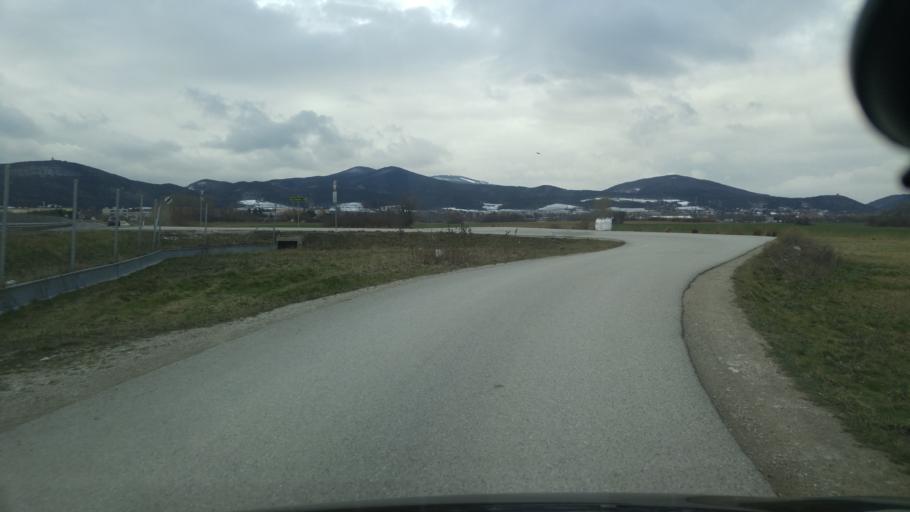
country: AT
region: Lower Austria
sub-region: Politischer Bezirk Baden
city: Bad Voslau
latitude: 47.9751
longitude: 16.2373
